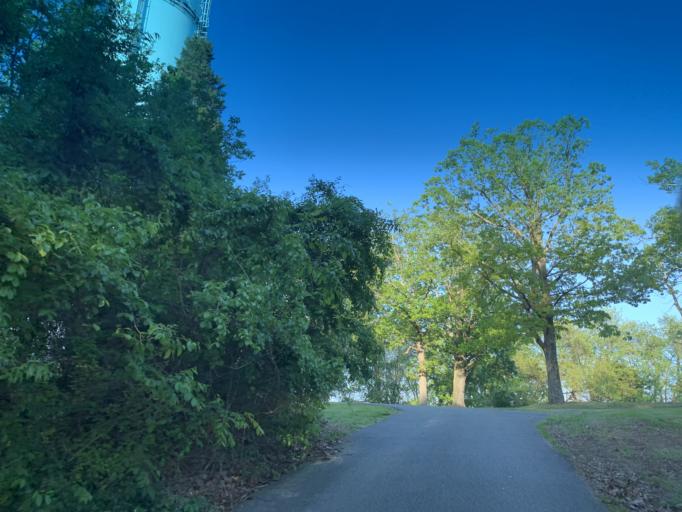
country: US
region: Maryland
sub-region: Harford County
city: Aberdeen
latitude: 39.5230
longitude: -76.1926
